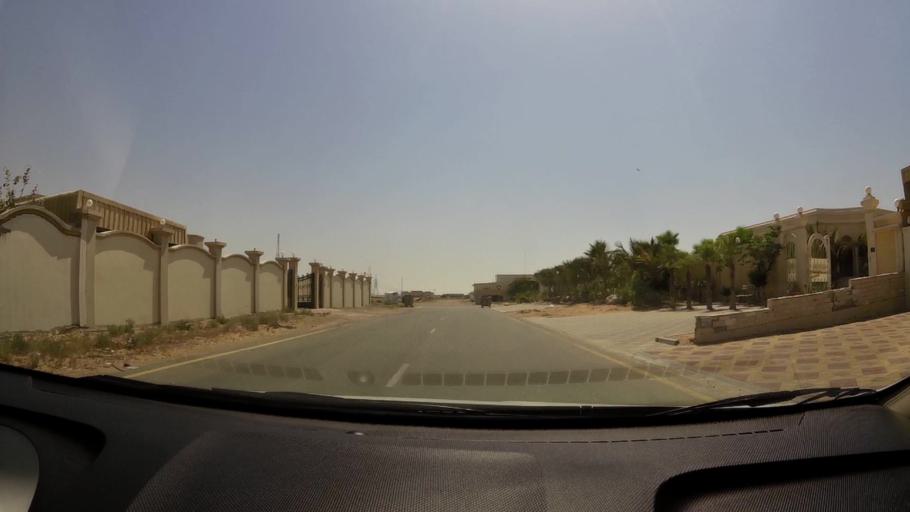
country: AE
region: Umm al Qaywayn
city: Umm al Qaywayn
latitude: 25.4908
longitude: 55.5851
